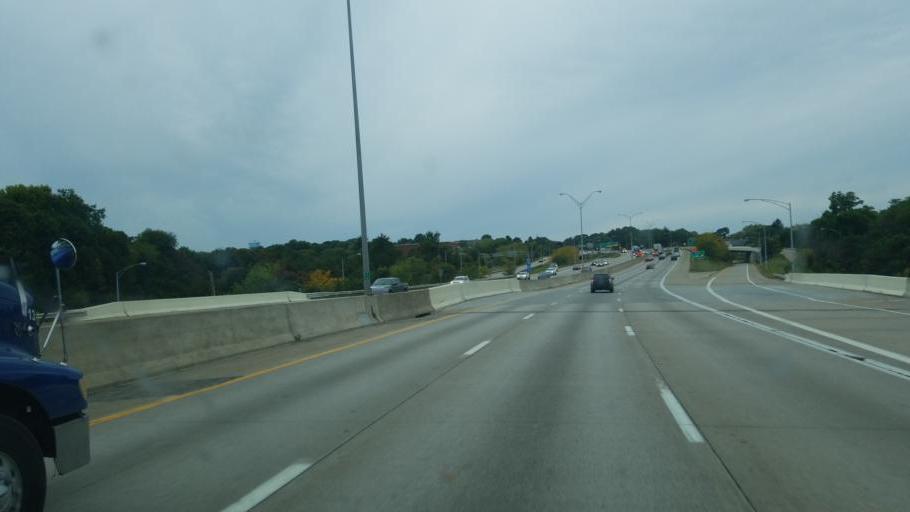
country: US
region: Ohio
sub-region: Summit County
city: Akron
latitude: 41.0625
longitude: -81.4832
